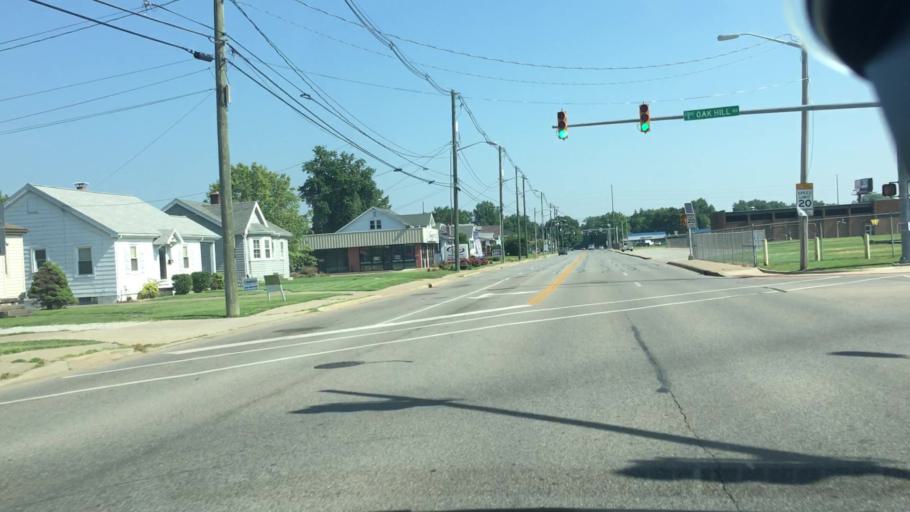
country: US
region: Indiana
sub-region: Vanderburgh County
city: Evansville
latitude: 37.9888
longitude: -87.5292
